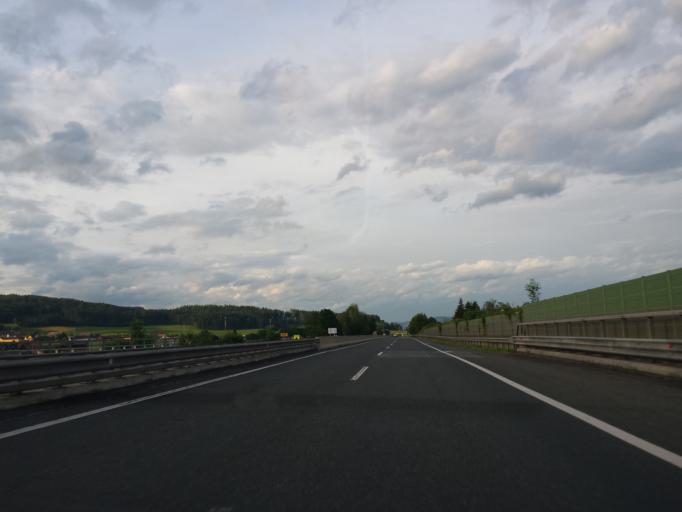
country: AT
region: Styria
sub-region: Politischer Bezirk Murtal
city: Spielberg bei Knittelfeld
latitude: 47.2164
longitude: 14.7997
